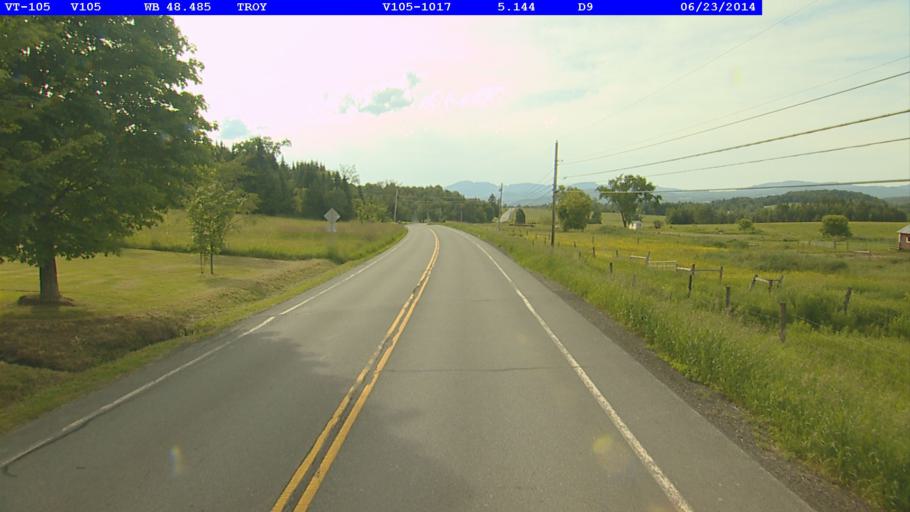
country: US
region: Vermont
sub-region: Orleans County
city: Newport
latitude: 44.9835
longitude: -72.3581
